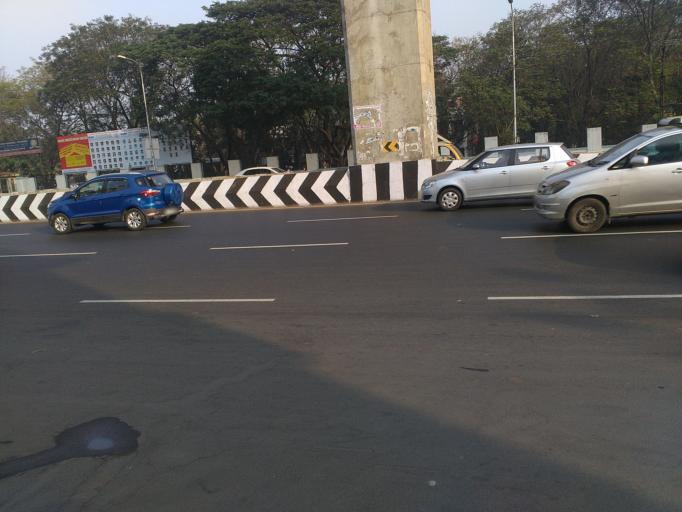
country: IN
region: Tamil Nadu
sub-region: Kancheepuram
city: Alandur
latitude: 13.0076
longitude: 80.2069
